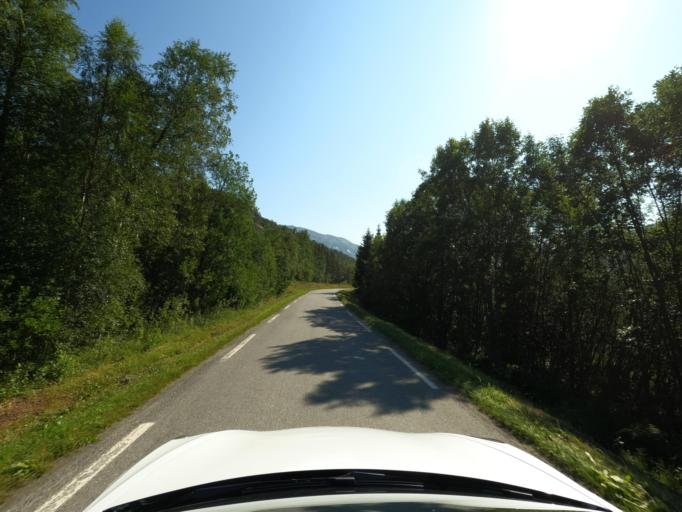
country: NO
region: Nordland
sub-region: Narvik
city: Narvik
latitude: 68.1855
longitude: 17.5559
